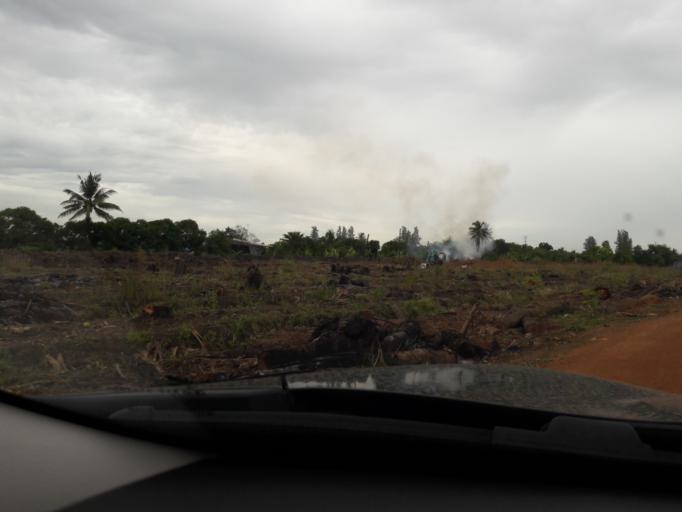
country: TH
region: Ratchaburi
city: Bang Phae
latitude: 13.6170
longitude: 99.9643
